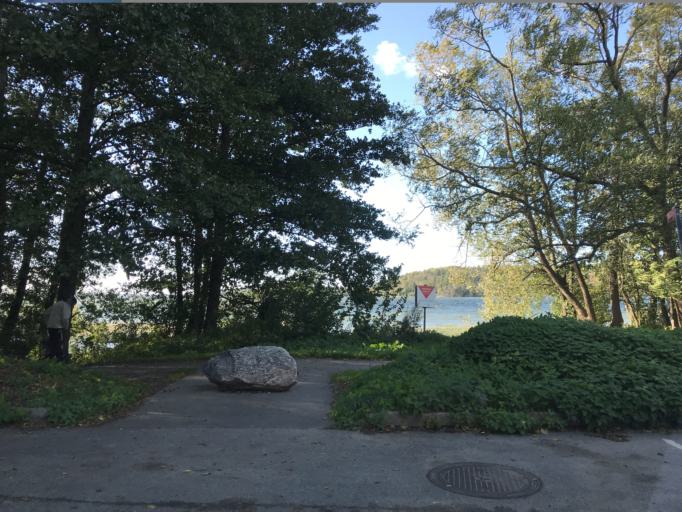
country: SE
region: Stockholm
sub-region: Huddinge Kommun
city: Segeltorp
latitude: 59.2858
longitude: 17.8920
